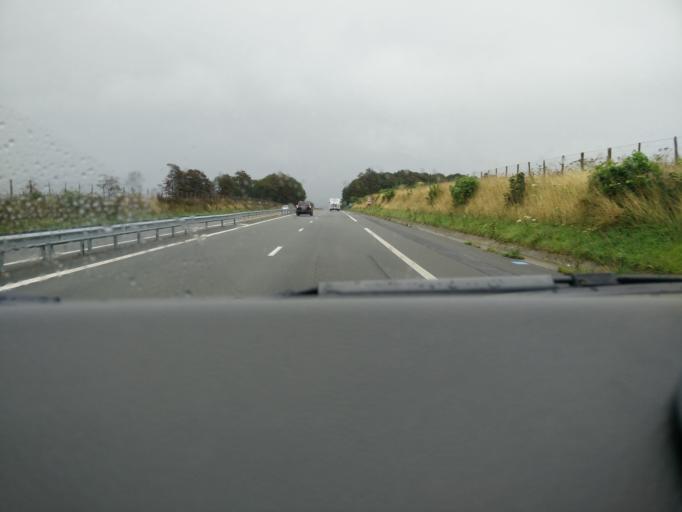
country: FR
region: Nord-Pas-de-Calais
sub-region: Departement du Pas-de-Calais
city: Marconnelle
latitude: 50.3614
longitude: 1.9937
